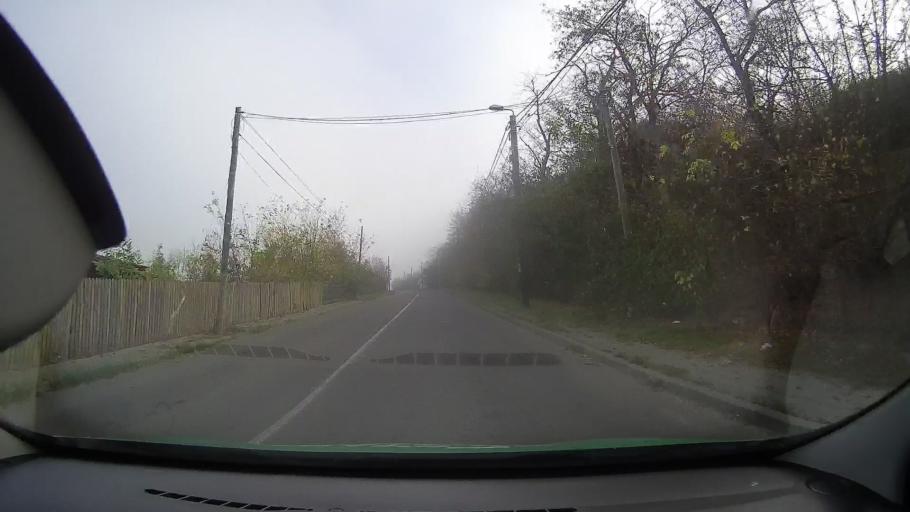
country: RO
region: Tulcea
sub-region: Municipiul Tulcea
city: Tulcea
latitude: 45.1655
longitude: 28.8274
